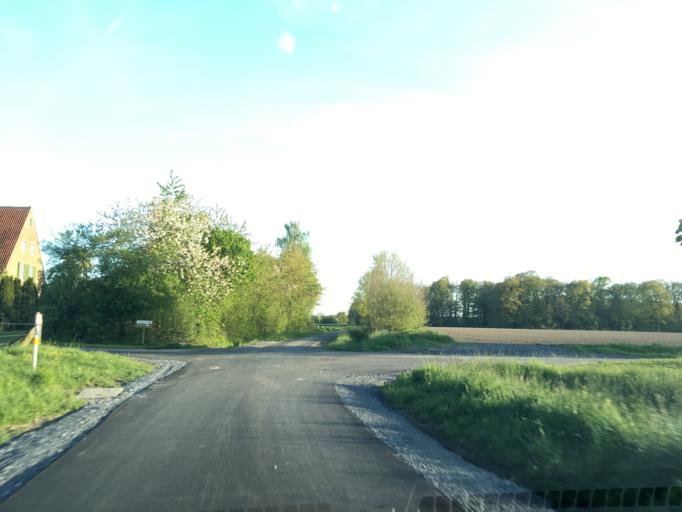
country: DE
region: North Rhine-Westphalia
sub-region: Regierungsbezirk Munster
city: Muenster
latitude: 52.0209
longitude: 7.6130
